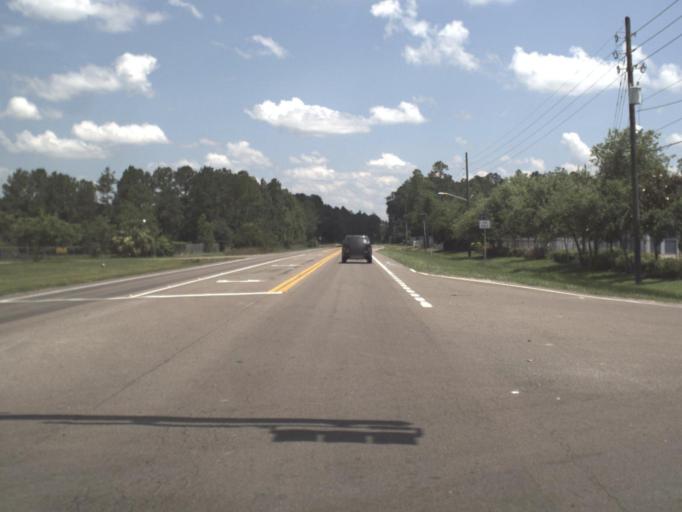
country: US
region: Florida
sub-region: Alachua County
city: Gainesville
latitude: 29.7161
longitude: -82.3536
